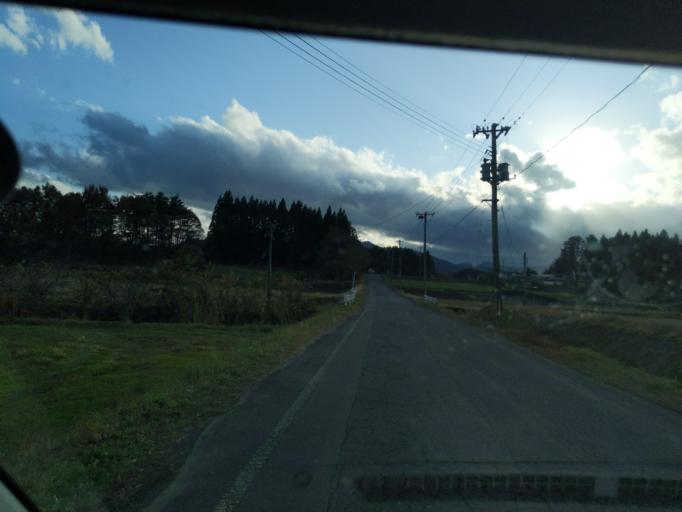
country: JP
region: Iwate
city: Mizusawa
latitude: 39.1081
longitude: 141.0002
